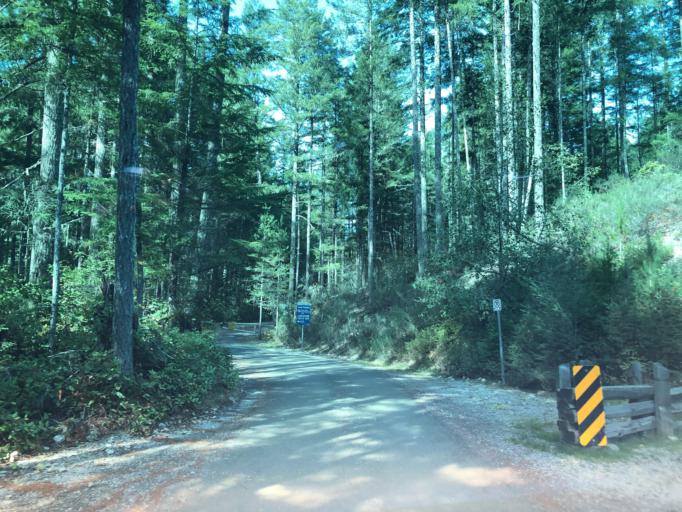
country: CA
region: British Columbia
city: Sooke
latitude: 48.4432
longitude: -123.7211
